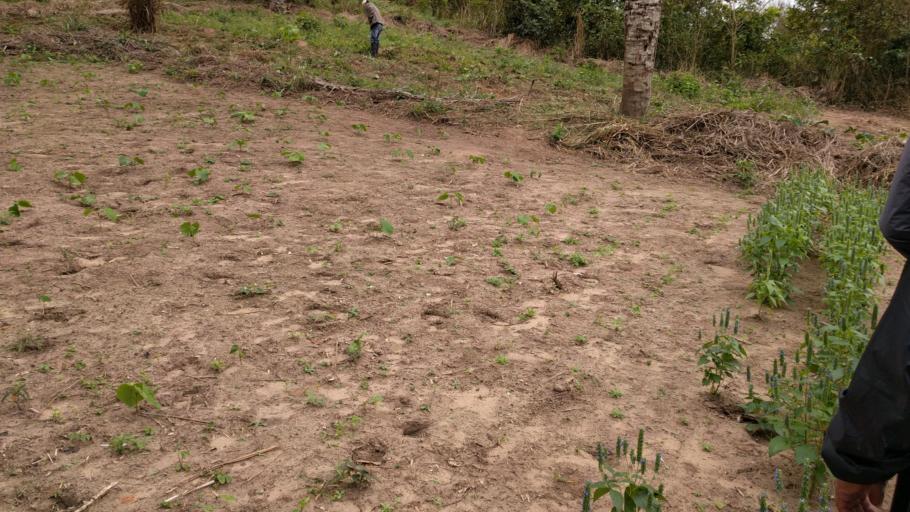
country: BO
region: Santa Cruz
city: San Juan del Surutu
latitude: -17.4578
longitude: -63.6959
